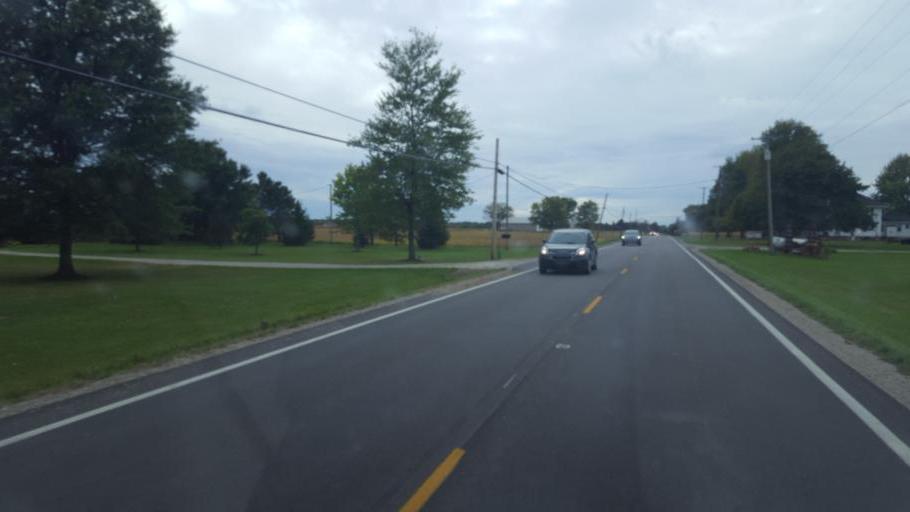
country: US
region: Ohio
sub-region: Lorain County
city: South Amherst
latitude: 41.3398
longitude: -82.3107
